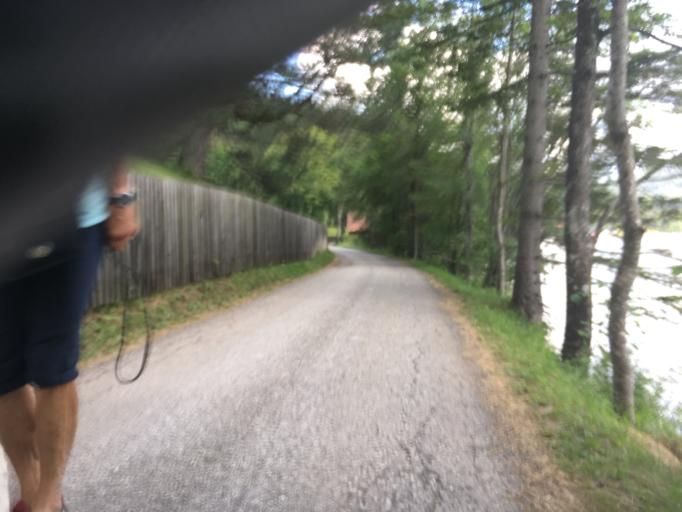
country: AT
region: Lower Austria
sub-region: Politischer Bezirk Lilienfeld
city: Mitterbach am Erlaufsee
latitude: 47.7952
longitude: 15.2708
